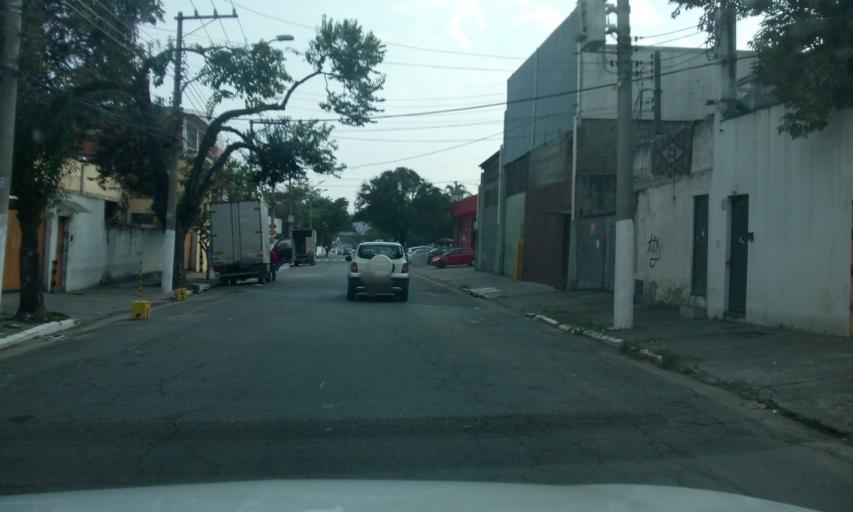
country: BR
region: Sao Paulo
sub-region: Osasco
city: Osasco
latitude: -23.5346
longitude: -46.7303
